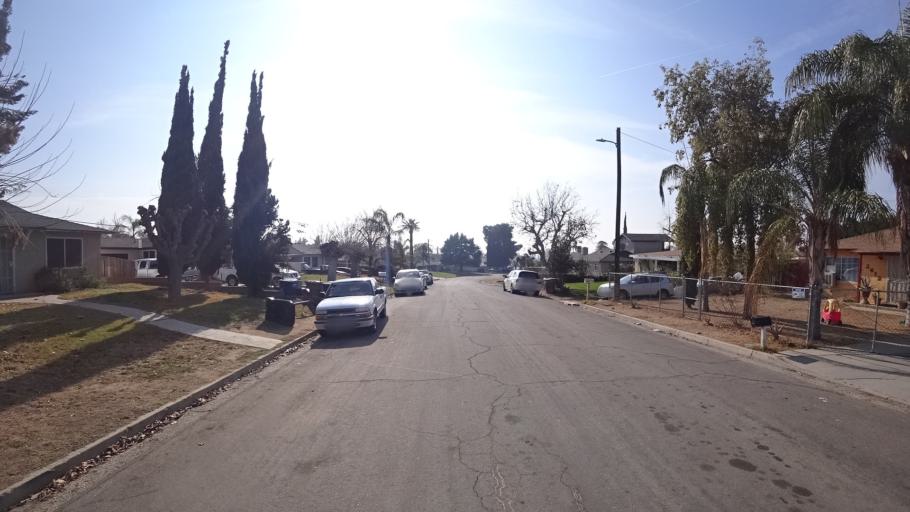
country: US
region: California
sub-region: Kern County
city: Bakersfield
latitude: 35.3919
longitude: -118.9706
